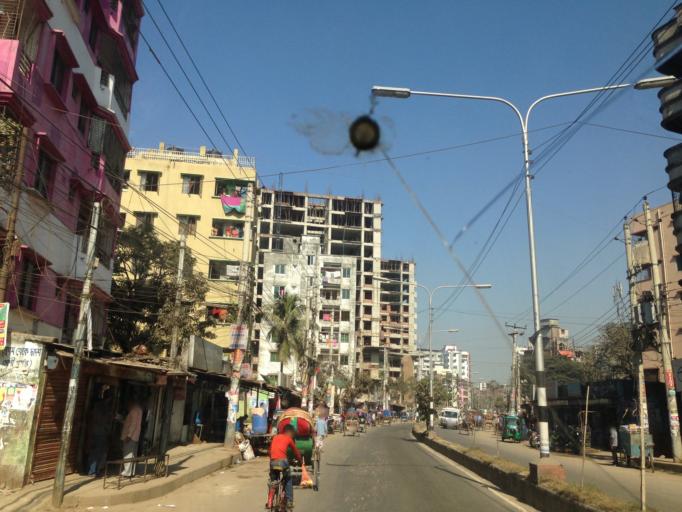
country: BD
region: Dhaka
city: Azimpur
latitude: 23.8118
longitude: 90.3608
